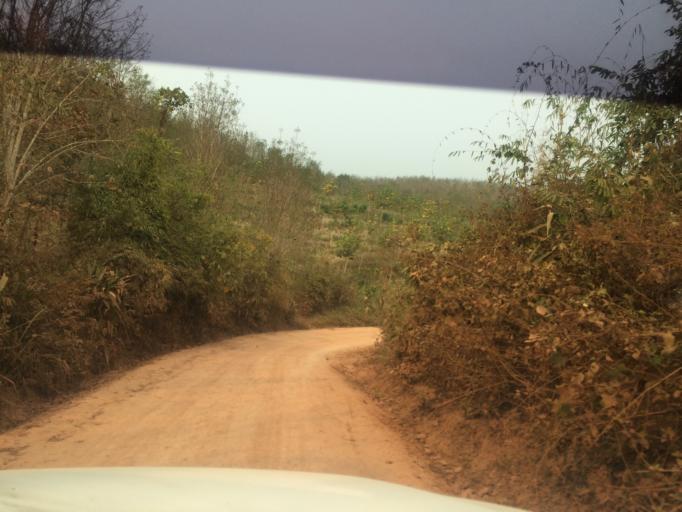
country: LA
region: Loungnamtha
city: Muang Nale
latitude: 20.4197
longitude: 101.6991
